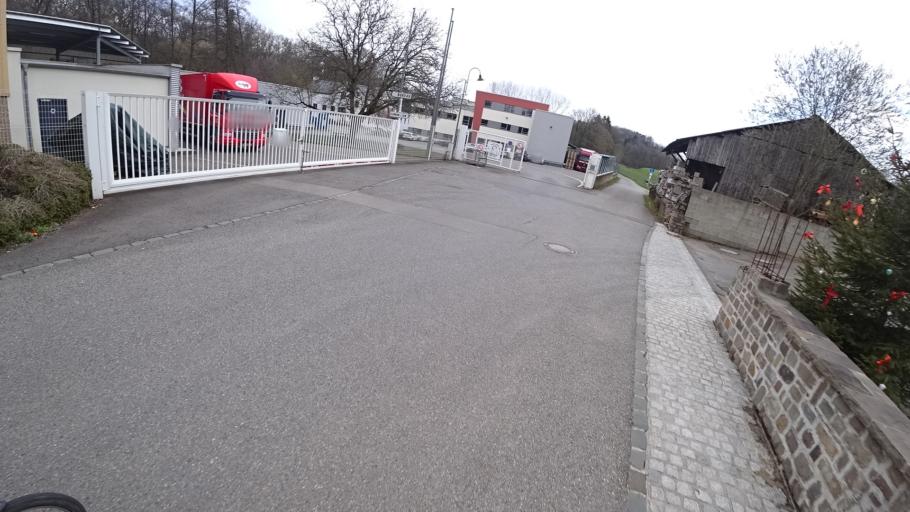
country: LU
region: Diekirch
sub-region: Canton de Redange
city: Useldange
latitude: 49.7695
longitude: 5.9904
